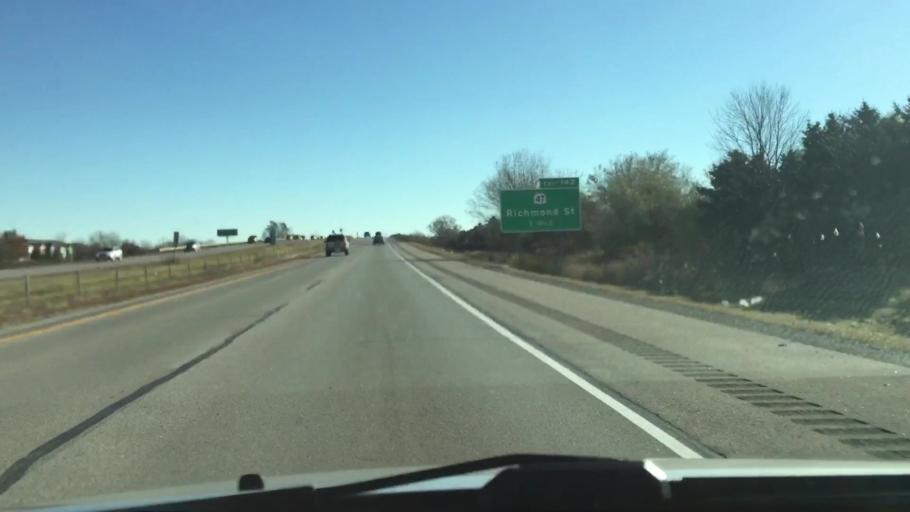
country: US
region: Wisconsin
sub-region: Outagamie County
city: Appleton
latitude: 44.2989
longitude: -88.4420
